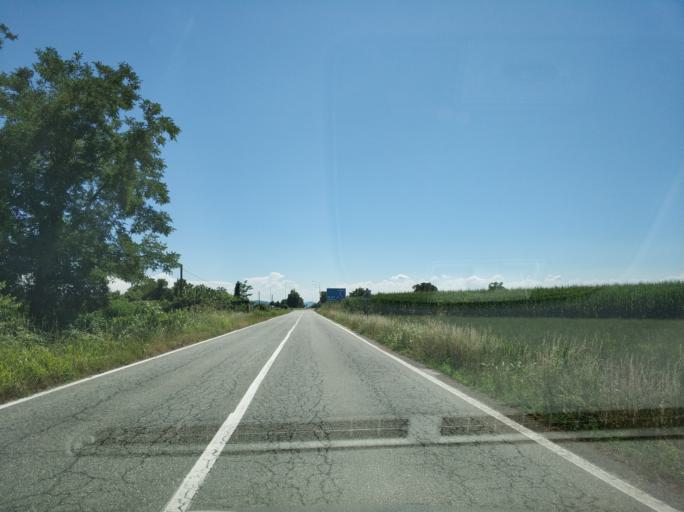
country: IT
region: Piedmont
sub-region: Provincia di Vercelli
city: Cigliano
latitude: 45.3005
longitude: 8.0087
